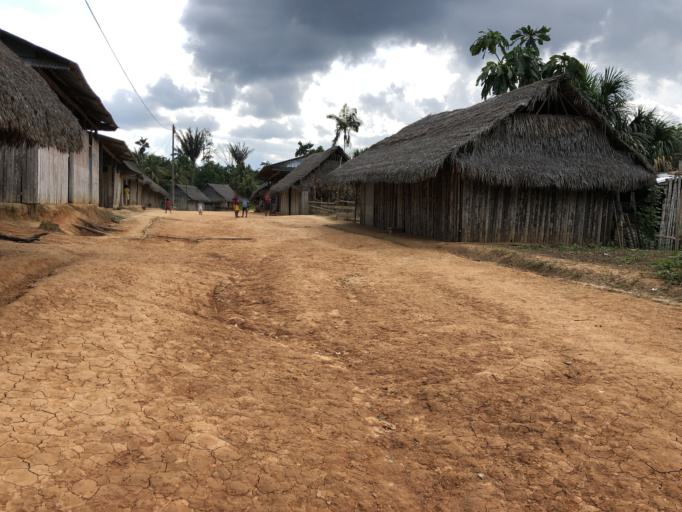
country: PE
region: Loreto
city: Puerto Galilea
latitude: -4.0543
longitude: -77.7576
